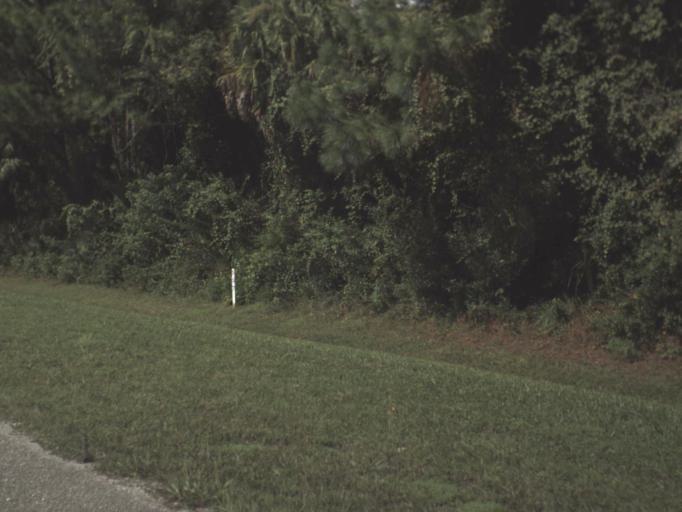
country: US
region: Florida
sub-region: Sarasota County
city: Vamo
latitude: 27.2378
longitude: -82.5025
